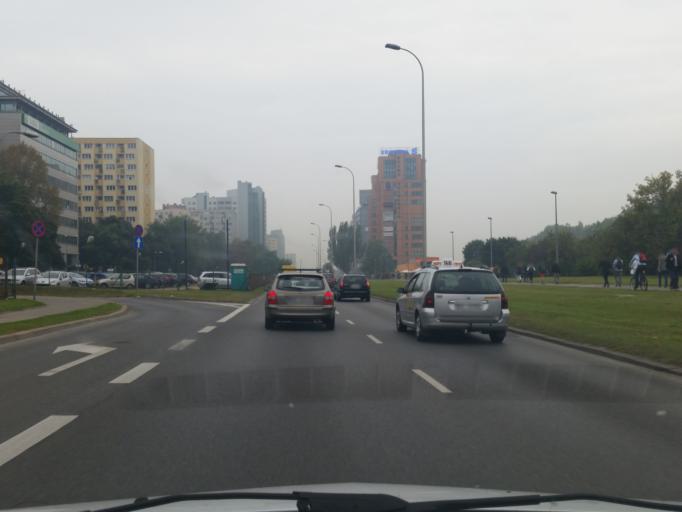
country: PL
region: Masovian Voivodeship
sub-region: Warszawa
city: Ochota
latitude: 52.2242
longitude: 20.9861
